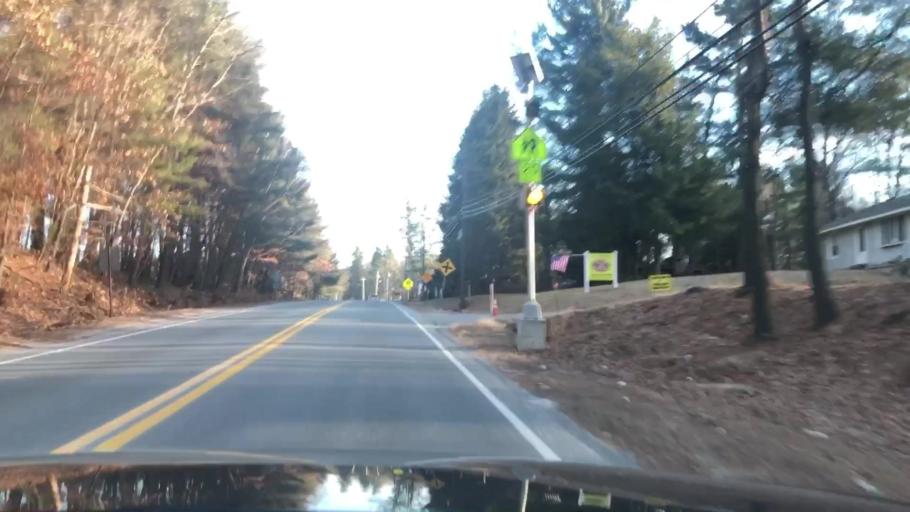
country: US
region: Massachusetts
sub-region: Worcester County
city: Bolton
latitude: 42.4512
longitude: -71.6370
